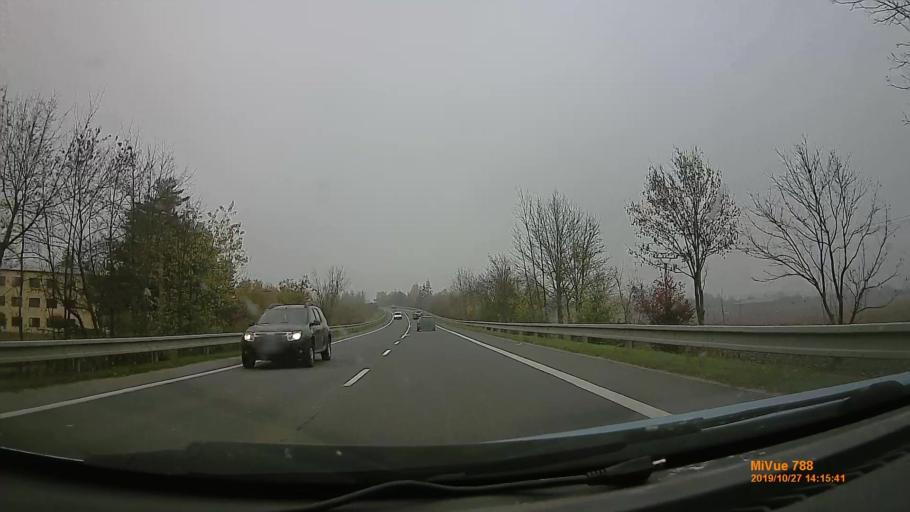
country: CZ
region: Olomoucky
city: Zabreh
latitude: 49.8833
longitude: 16.8934
